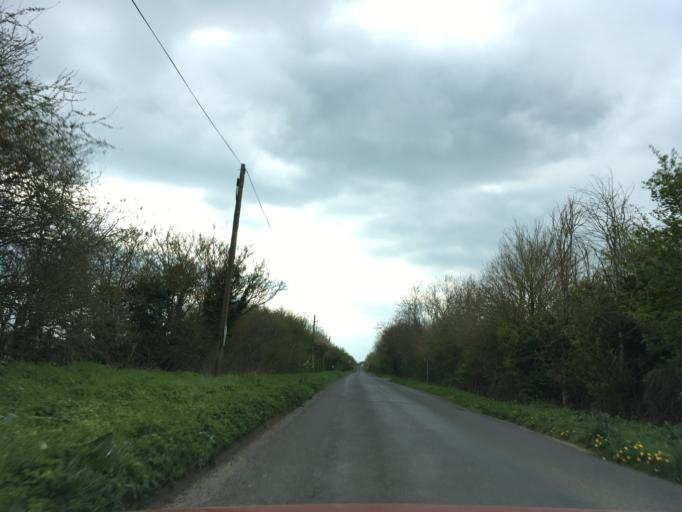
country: GB
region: England
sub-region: Oxfordshire
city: Bicester
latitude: 51.8860
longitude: -1.1967
